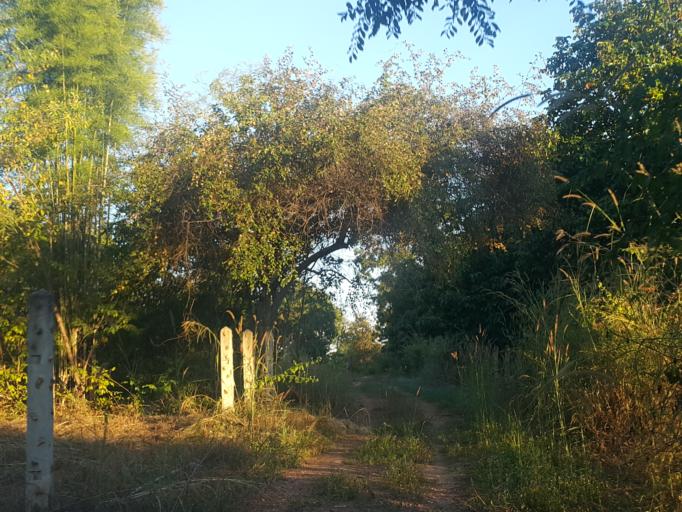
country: TH
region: Chiang Mai
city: San Sai
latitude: 18.8657
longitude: 99.1451
